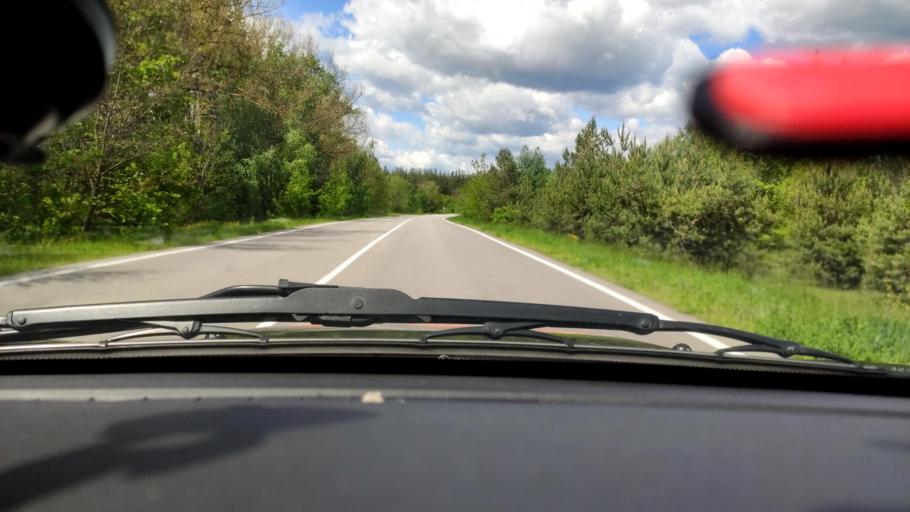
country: RU
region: Belgorod
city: Krasnoye
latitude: 51.0568
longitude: 38.8511
